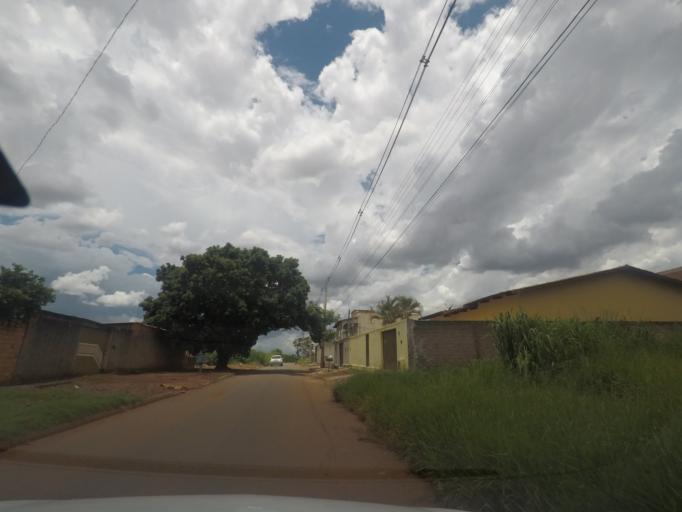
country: BR
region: Goias
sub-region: Goiania
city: Goiania
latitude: -16.7101
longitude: -49.3447
